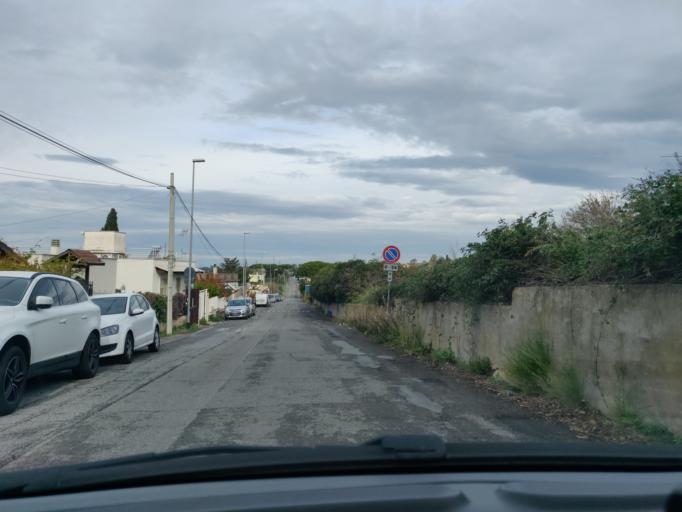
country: IT
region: Latium
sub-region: Citta metropolitana di Roma Capitale
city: Civitavecchia
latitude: 42.0994
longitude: 11.8137
